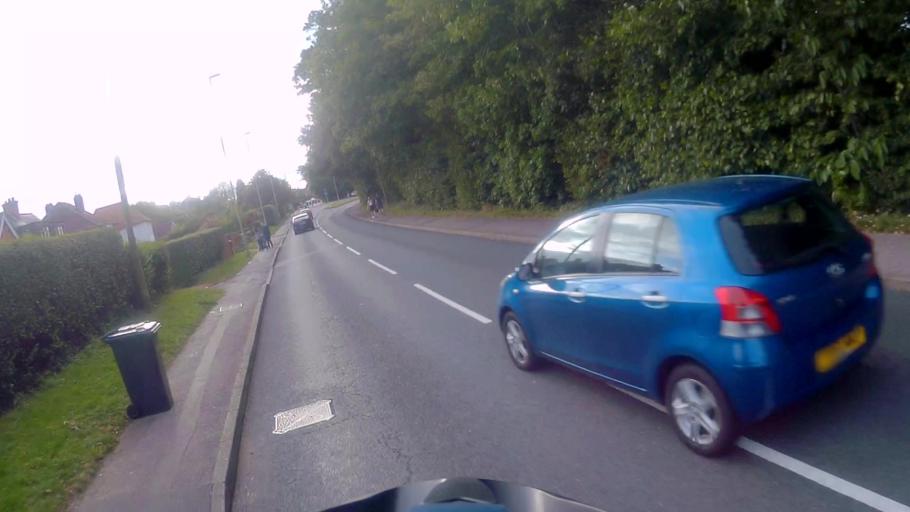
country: GB
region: England
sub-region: Hampshire
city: Basingstoke
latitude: 51.2619
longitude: -1.1139
